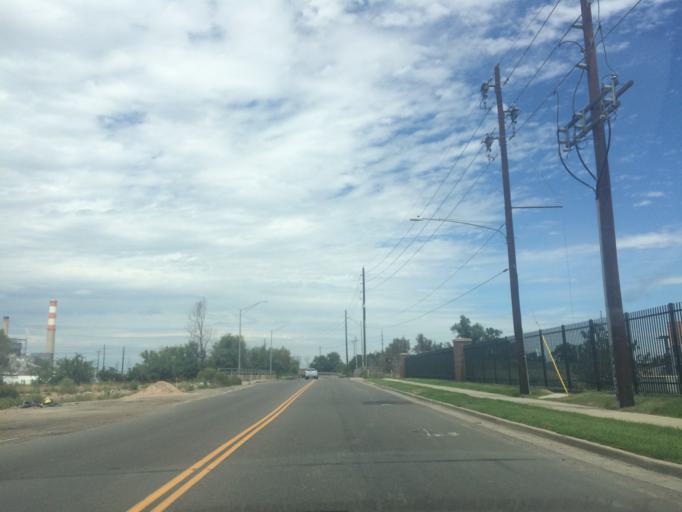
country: US
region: Colorado
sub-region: Adams County
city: Commerce City
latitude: 39.7997
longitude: -104.9594
